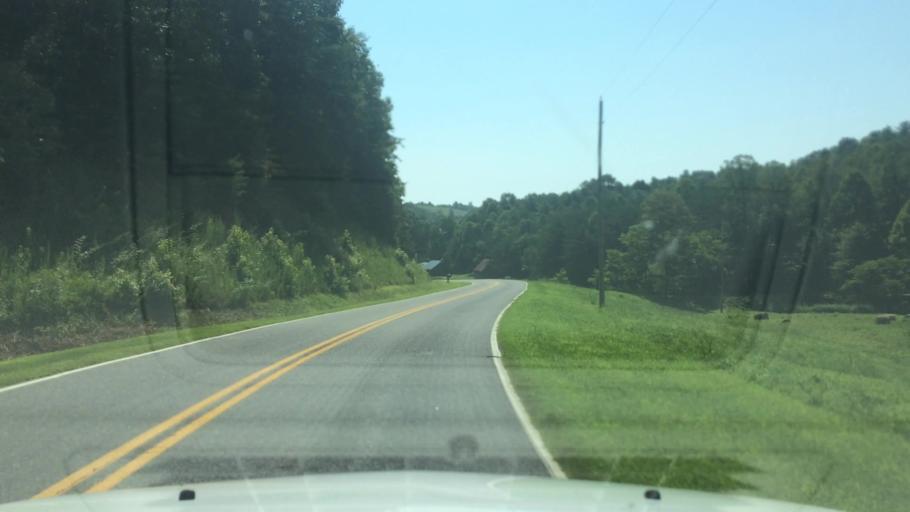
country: US
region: North Carolina
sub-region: Alexander County
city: Taylorsville
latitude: 35.9947
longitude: -81.2739
